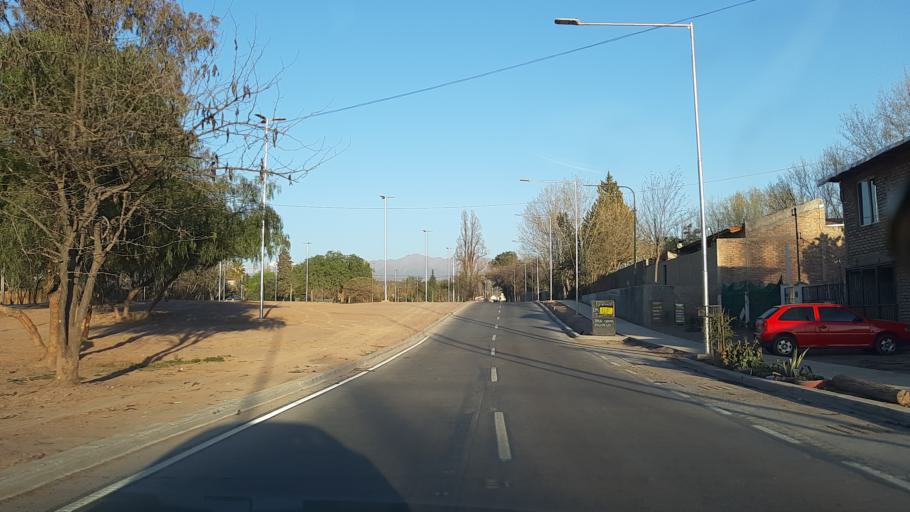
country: AR
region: Mendoza
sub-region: Departamento de Godoy Cruz
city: Godoy Cruz
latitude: -32.9650
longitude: -68.8565
